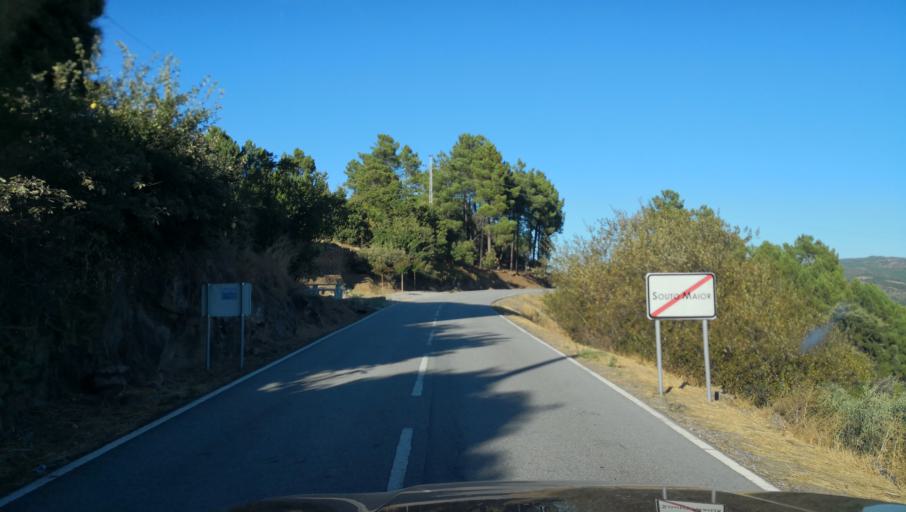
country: PT
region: Vila Real
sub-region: Sabrosa
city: Sabrosa
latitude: 41.3002
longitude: -7.5798
